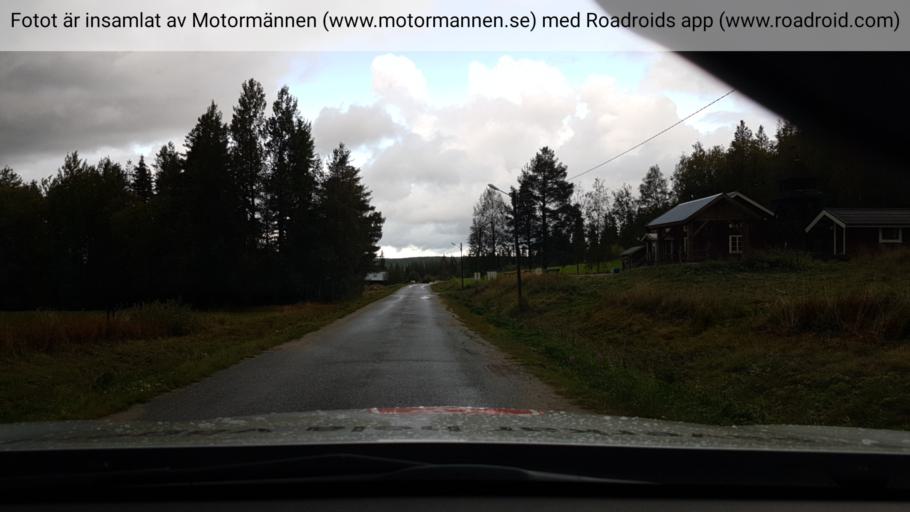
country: SE
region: Vaesterbotten
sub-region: Asele Kommun
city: Asele
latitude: 64.1900
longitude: 16.9183
